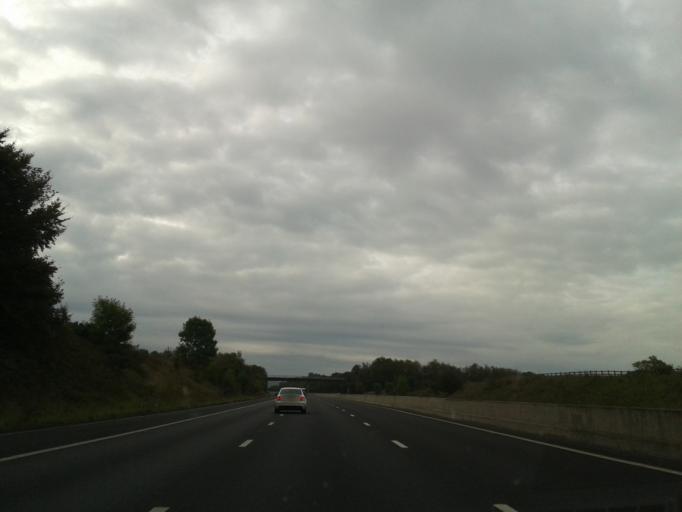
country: GB
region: England
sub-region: Cumbria
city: Scotby
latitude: 54.8289
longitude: -2.8895
